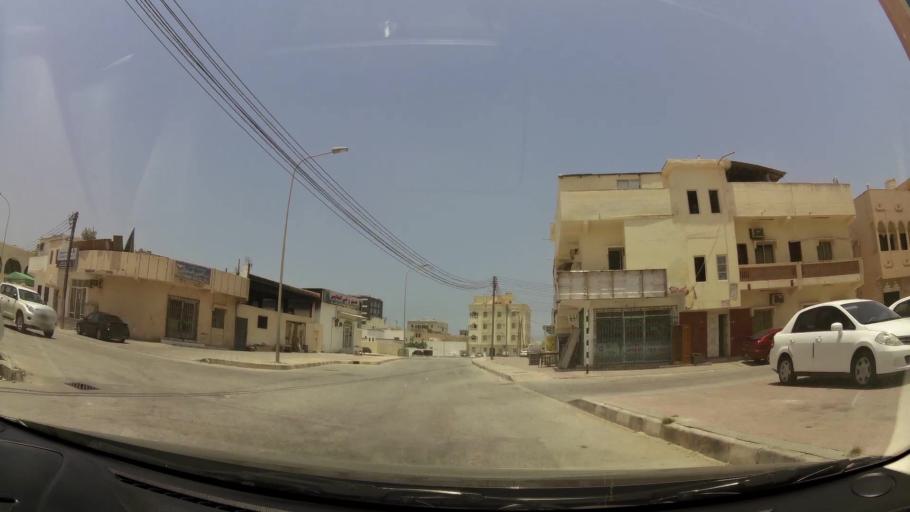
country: OM
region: Zufar
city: Salalah
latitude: 17.0182
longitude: 54.1081
